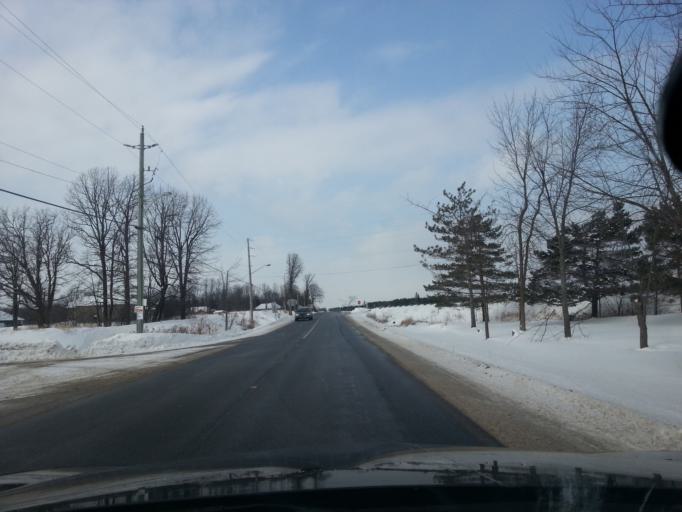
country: CA
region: Ontario
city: Carleton Place
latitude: 45.1588
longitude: -76.0351
